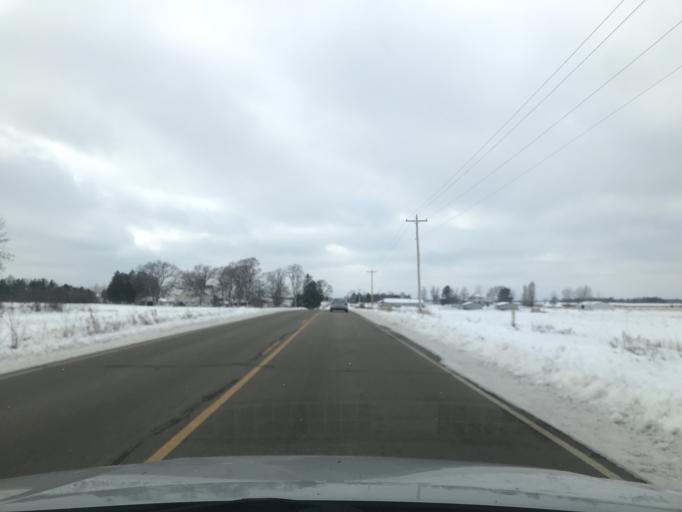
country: US
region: Wisconsin
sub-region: Oconto County
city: Oconto
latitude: 44.9499
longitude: -87.9133
